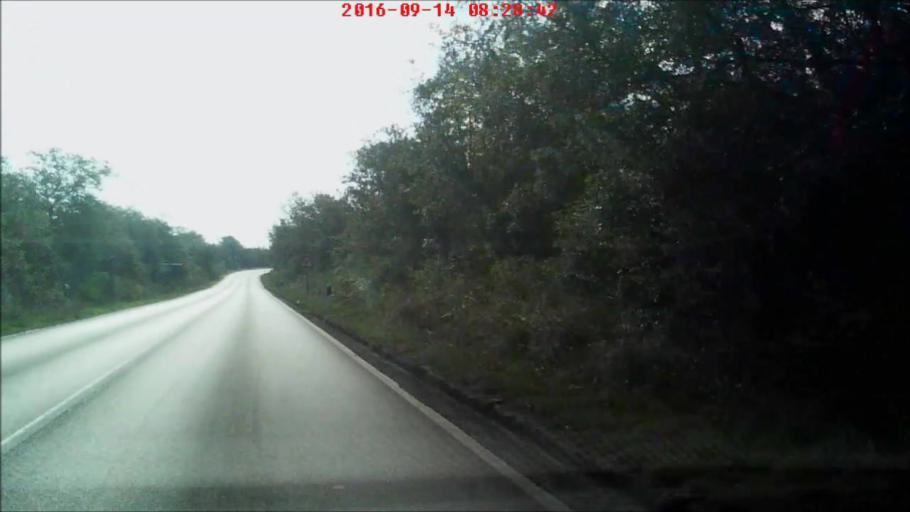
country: HR
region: Zadarska
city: Zadar
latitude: 44.1842
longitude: 15.2779
